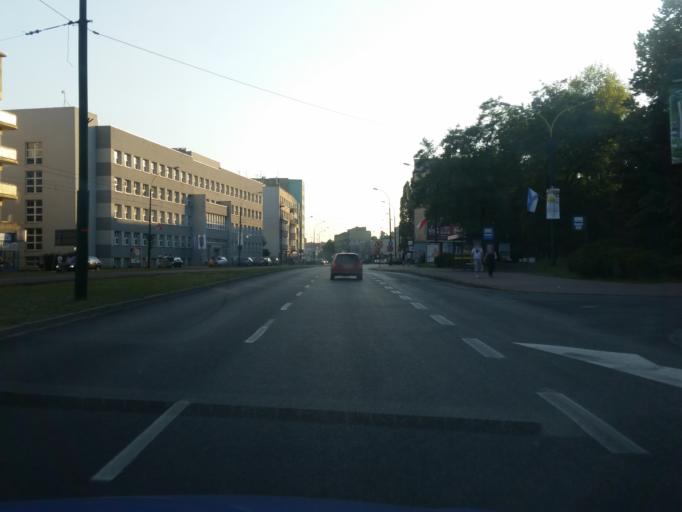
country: PL
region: Silesian Voivodeship
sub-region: Sosnowiec
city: Sosnowiec
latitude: 50.2811
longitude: 19.1341
